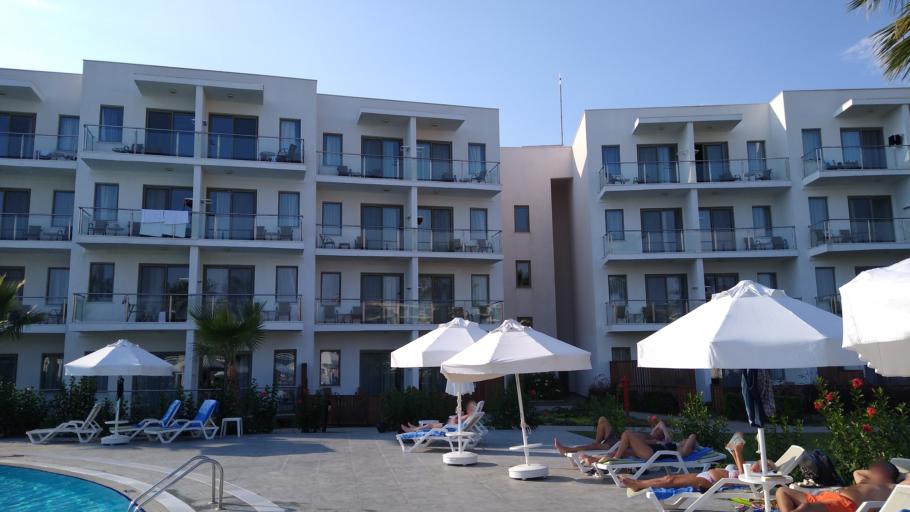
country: TR
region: Antalya
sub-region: Manavgat
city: Manavgat
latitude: 36.7514
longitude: 31.4529
